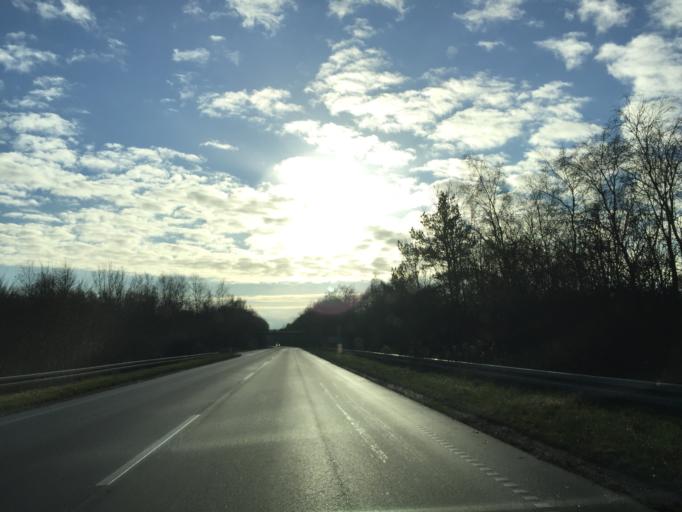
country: DK
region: Central Jutland
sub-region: Arhus Kommune
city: Framlev
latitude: 56.1877
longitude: 10.0055
